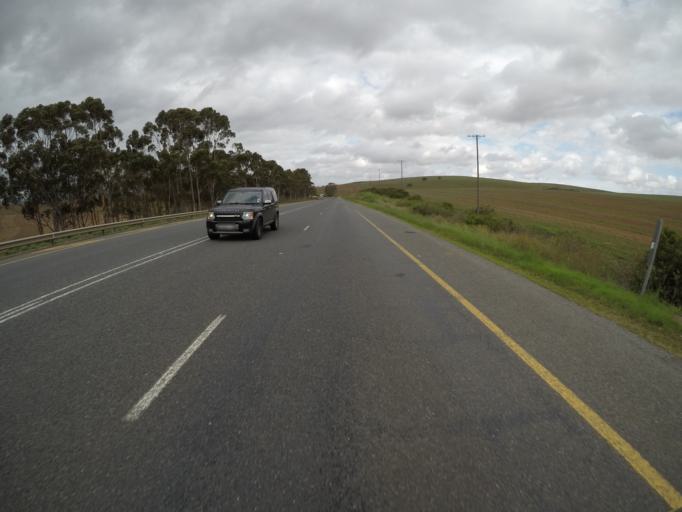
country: ZA
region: Western Cape
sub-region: Eden District Municipality
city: Riversdale
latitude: -34.1182
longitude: 20.8707
